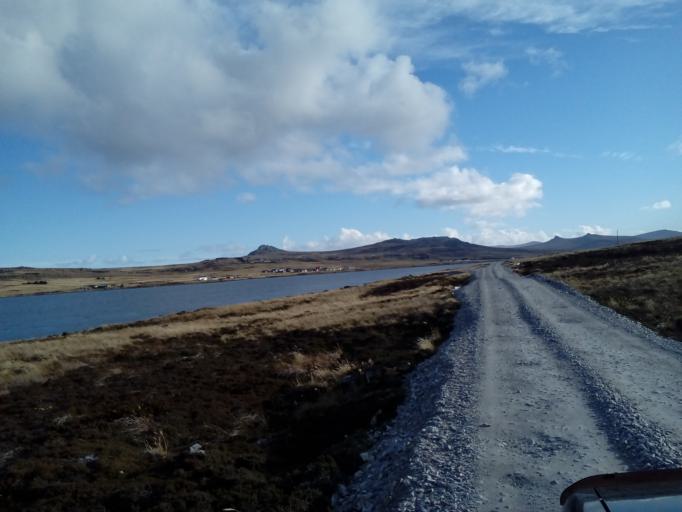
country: FK
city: Stanley
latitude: -51.6838
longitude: -57.8895
